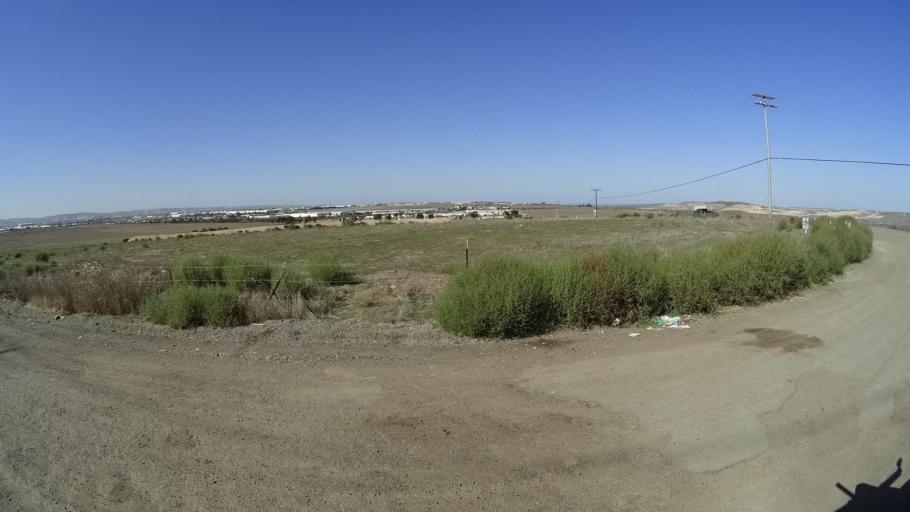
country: MX
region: Baja California
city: Tijuana
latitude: 32.5781
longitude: -116.9452
